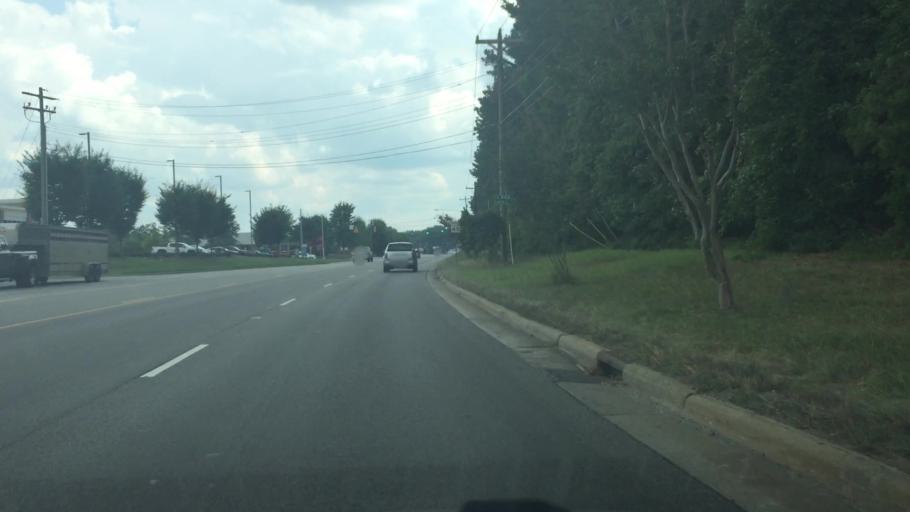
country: US
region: North Carolina
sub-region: Rowan County
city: Salisbury
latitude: 35.6703
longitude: -80.4997
